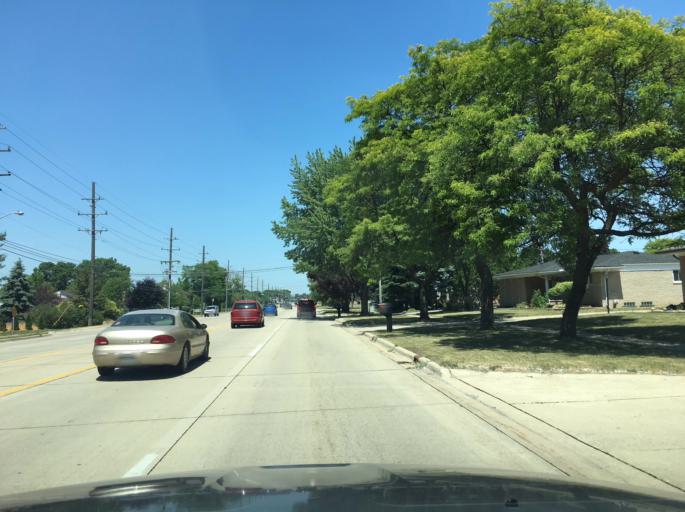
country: US
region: Michigan
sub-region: Macomb County
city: Fraser
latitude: 42.5594
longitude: -82.9505
